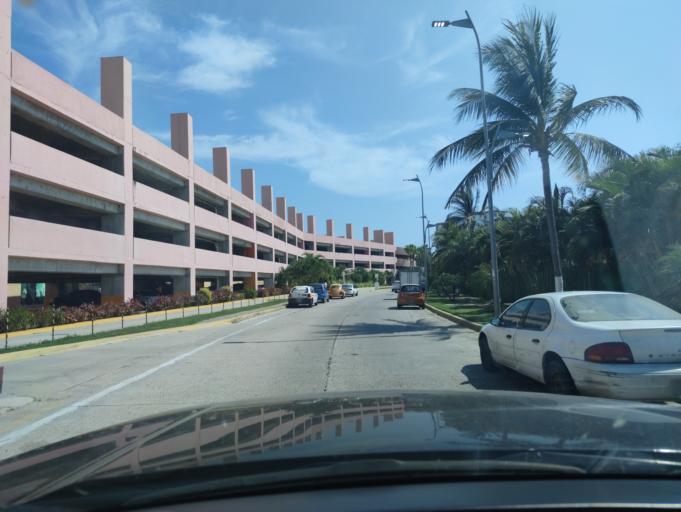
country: MX
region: Guerrero
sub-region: Acapulco de Juarez
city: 10 de Abril
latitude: 16.7730
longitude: -99.7774
